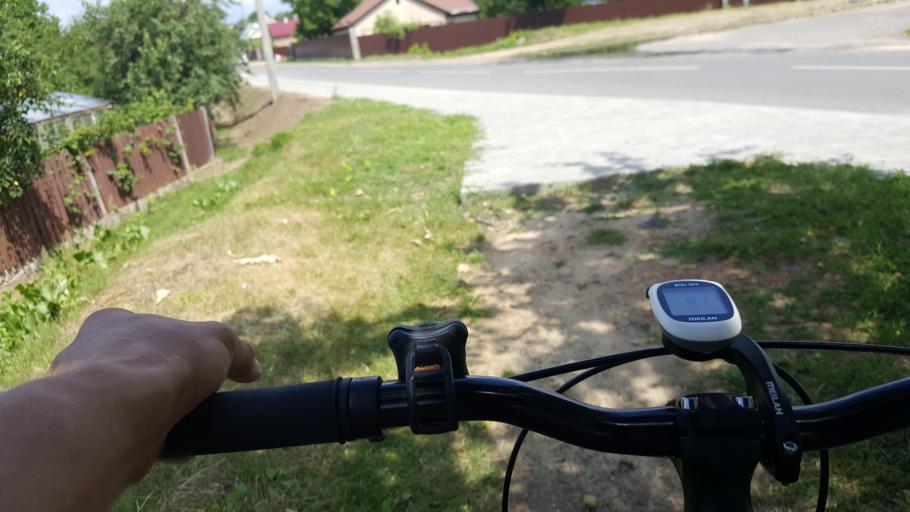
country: BY
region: Brest
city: Kamyanyets
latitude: 52.3983
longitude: 23.8264
